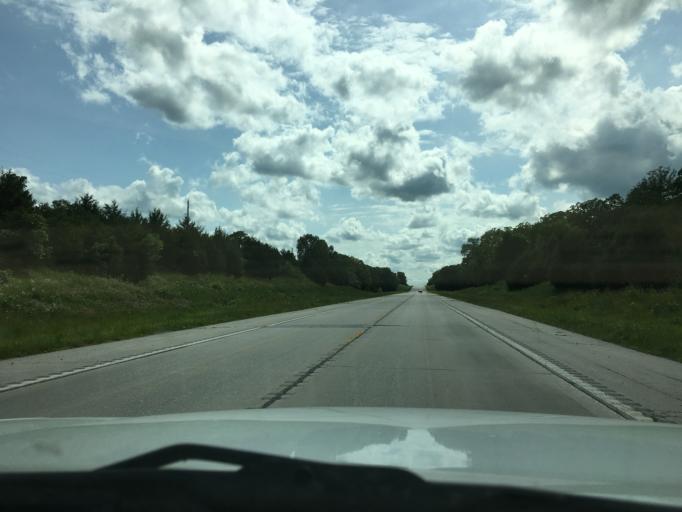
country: US
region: Missouri
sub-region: Franklin County
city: Gerald
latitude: 38.4216
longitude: -91.2839
